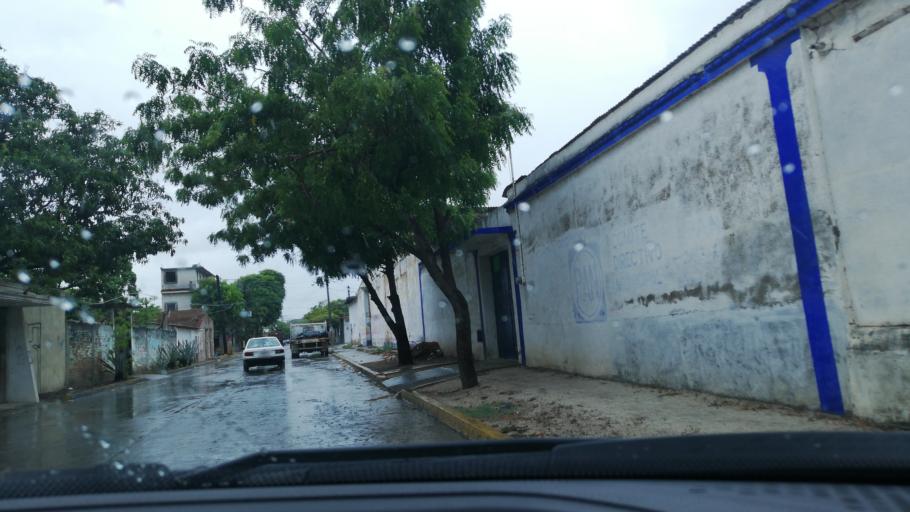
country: MX
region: Oaxaca
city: San Jeronimo Ixtepec
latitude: 16.5543
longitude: -95.0982
